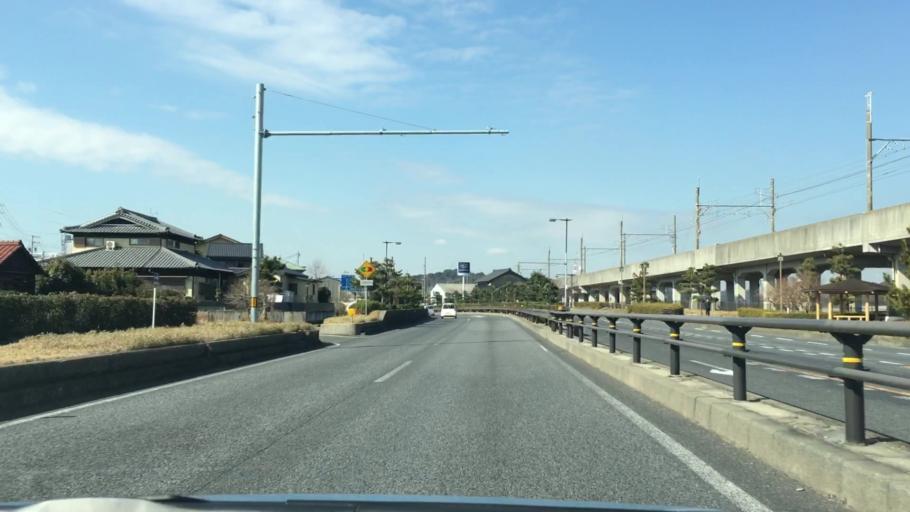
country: JP
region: Aichi
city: Gamagori
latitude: 34.8936
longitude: 137.2585
